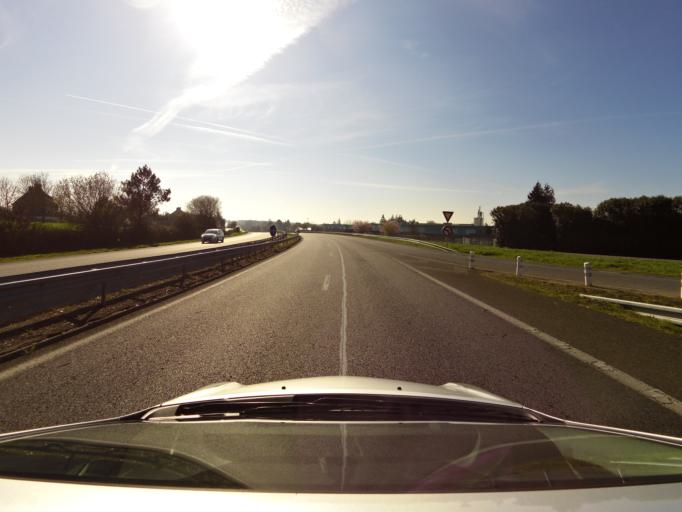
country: FR
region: Brittany
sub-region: Departement du Morbihan
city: Josselin
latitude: 47.9511
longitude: -2.5280
